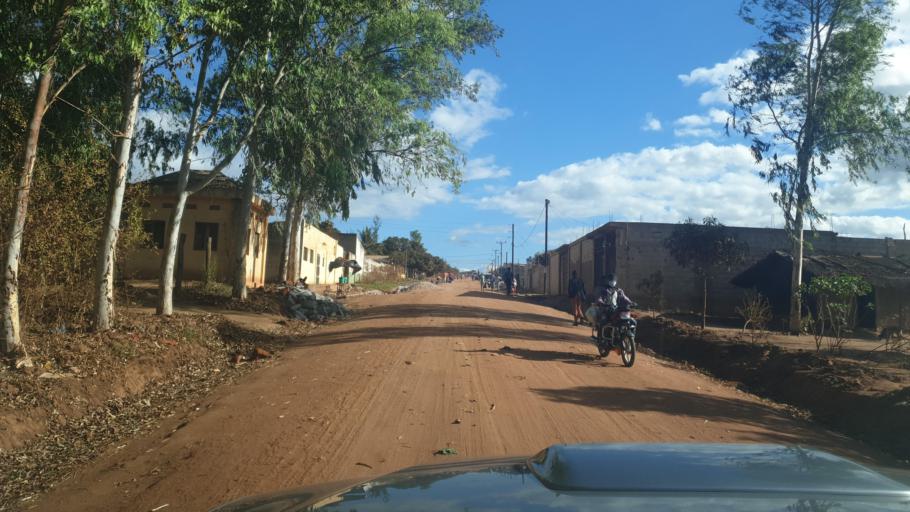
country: MZ
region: Nampula
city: Nampula
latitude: -15.0985
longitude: 39.2238
